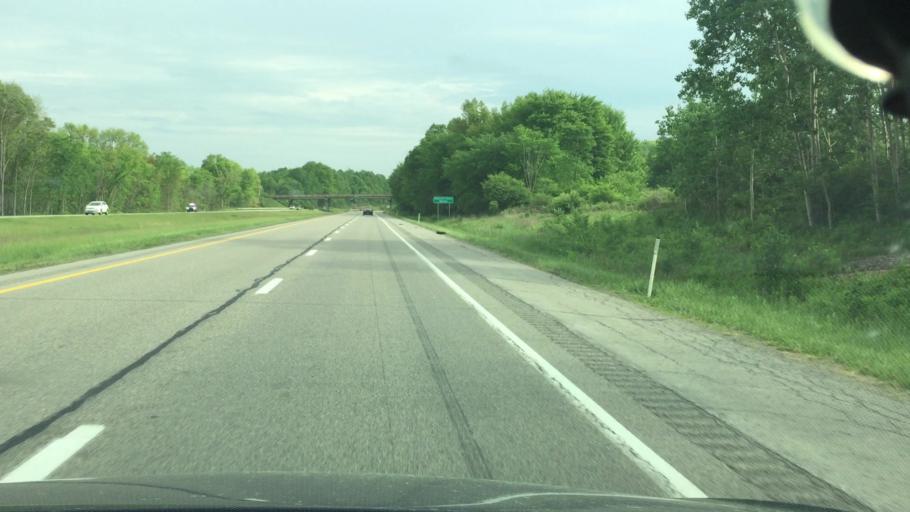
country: US
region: Pennsylvania
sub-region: Mercer County
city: Mercer
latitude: 41.2458
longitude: -80.1618
